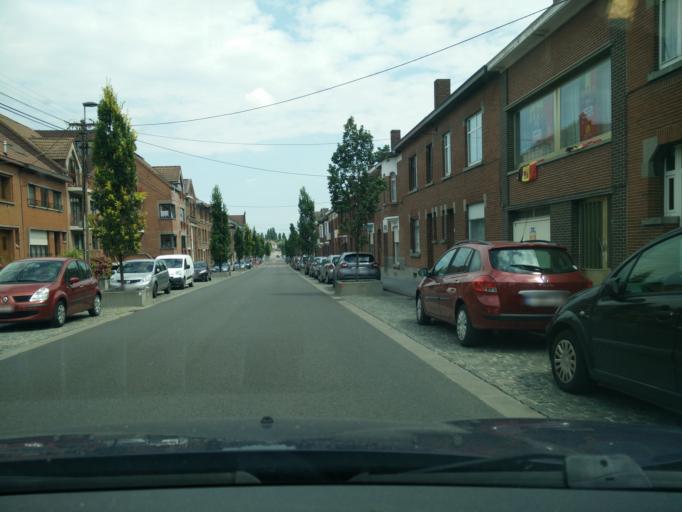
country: BE
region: Wallonia
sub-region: Province du Hainaut
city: Ecaussinnes-d'Enghien
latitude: 50.5653
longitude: 4.1628
